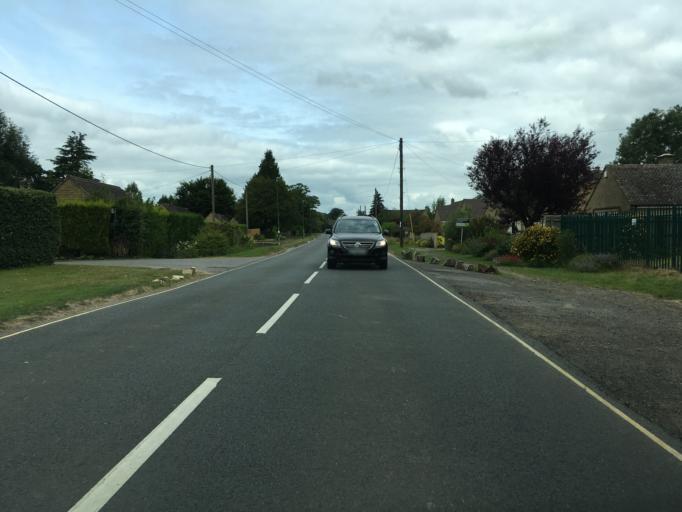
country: GB
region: England
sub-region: Gloucestershire
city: Bourton on the Water
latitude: 51.8762
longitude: -1.7416
